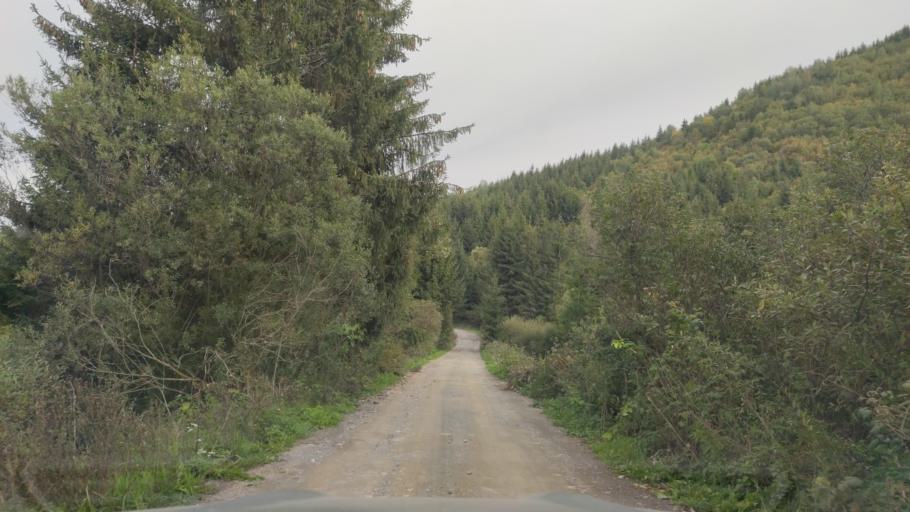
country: RO
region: Harghita
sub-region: Comuna Remetea
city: Remetea
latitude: 46.8118
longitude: 25.3615
